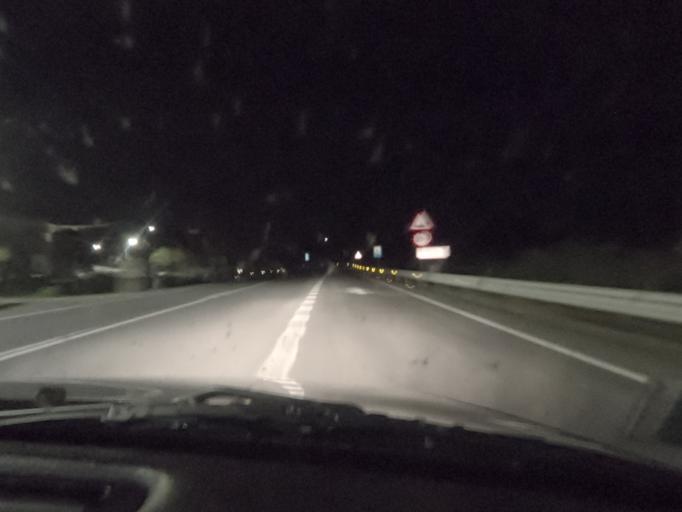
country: ES
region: Extremadura
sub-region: Provincia de Caceres
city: Perales del Puerto
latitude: 40.1531
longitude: -6.6791
